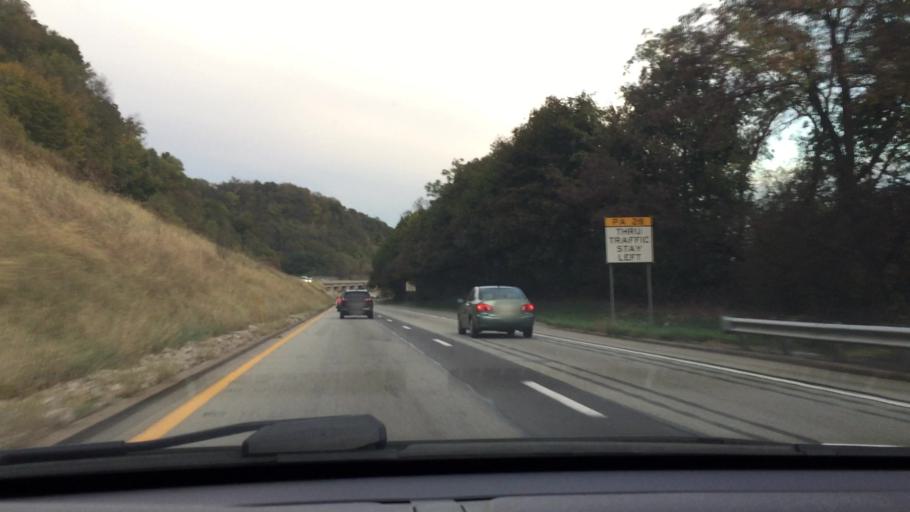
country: US
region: Pennsylvania
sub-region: Allegheny County
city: Sharpsburg
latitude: 40.4973
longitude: -79.9302
